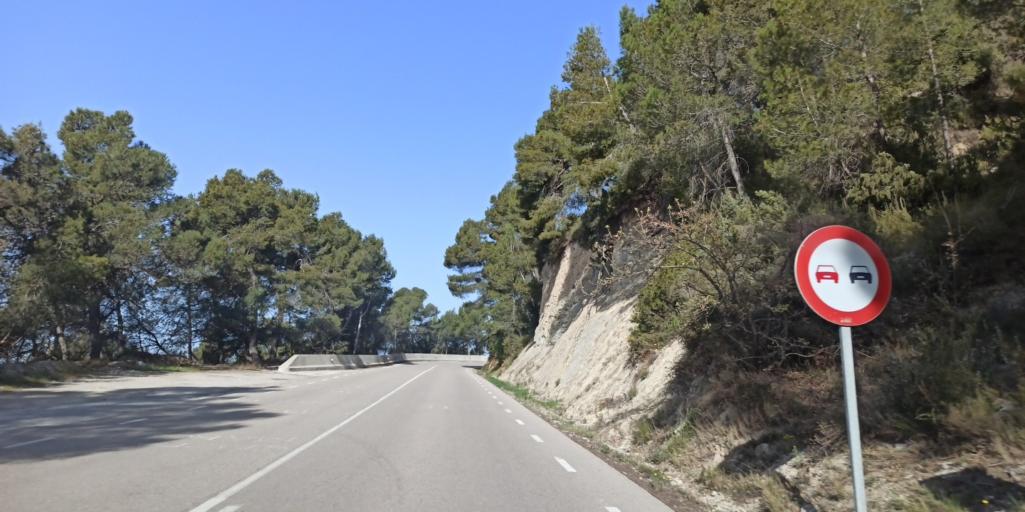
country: ES
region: Catalonia
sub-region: Provincia de Barcelona
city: Castelloli
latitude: 41.5958
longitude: 1.7240
